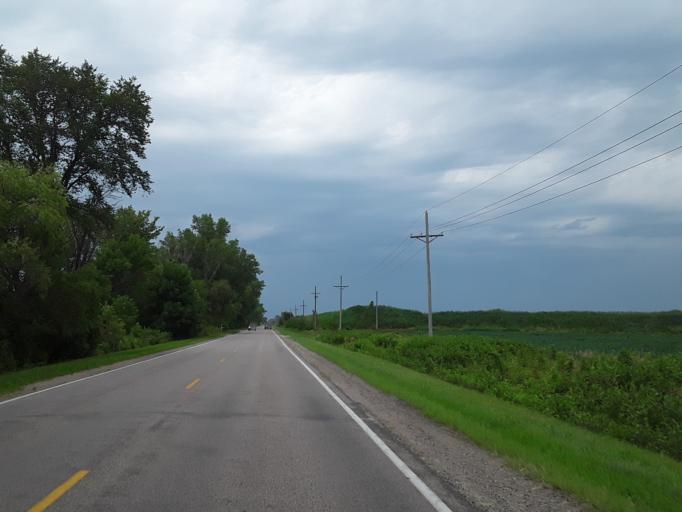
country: US
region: Nebraska
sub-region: Saunders County
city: Yutan
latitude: 41.2247
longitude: -96.3303
